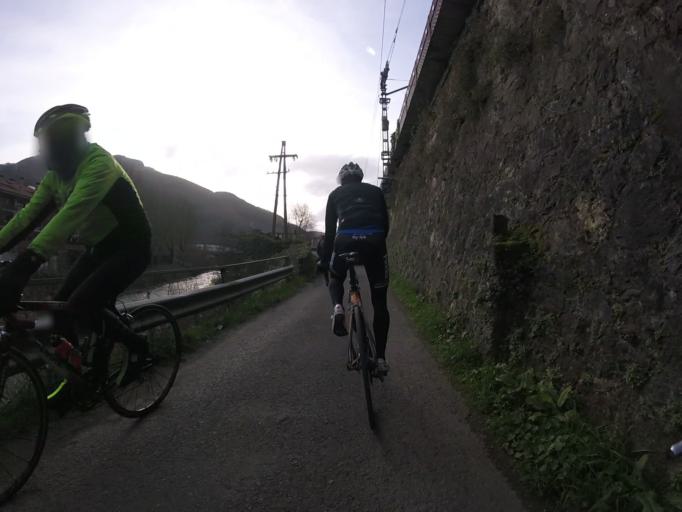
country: ES
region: Basque Country
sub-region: Provincia de Guipuzcoa
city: Anoeta
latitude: 43.1656
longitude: -2.0717
